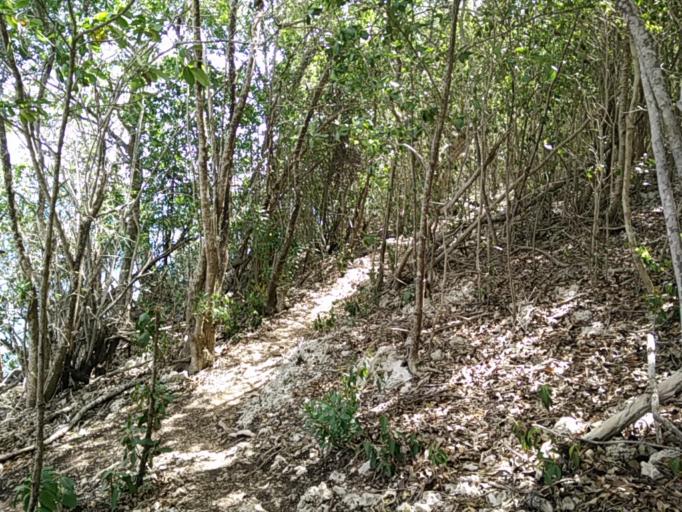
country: GP
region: Guadeloupe
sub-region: Guadeloupe
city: Sainte-Anne
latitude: 16.2107
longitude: -61.4287
